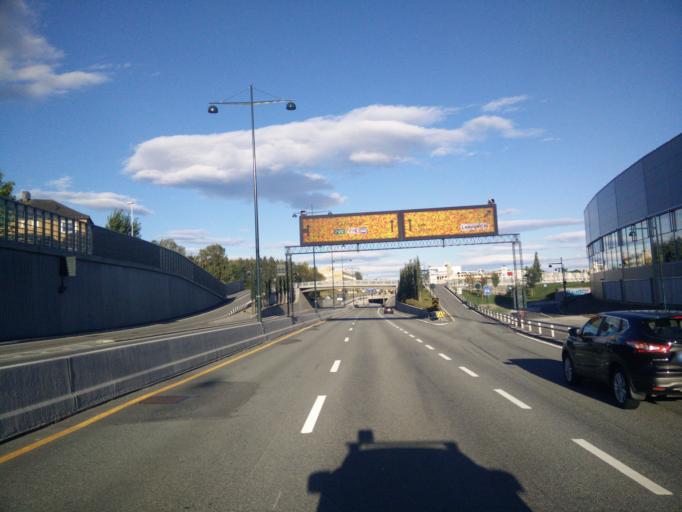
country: NO
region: Sor-Trondelag
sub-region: Trondheim
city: Trondheim
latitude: 63.4330
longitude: 10.4665
